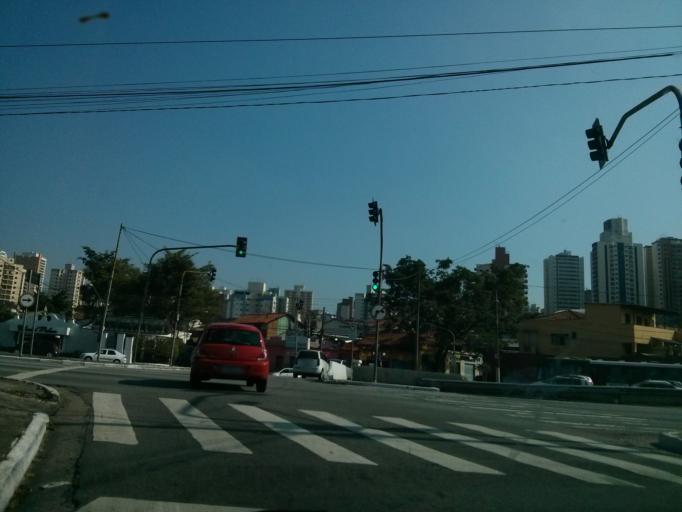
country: BR
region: Sao Paulo
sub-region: Sao Paulo
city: Sao Paulo
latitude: -23.6124
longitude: -46.6273
